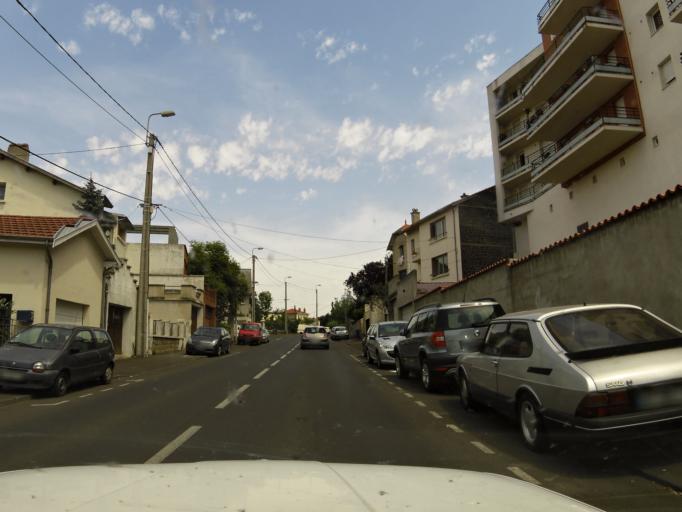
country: FR
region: Auvergne
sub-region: Departement du Puy-de-Dome
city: Beaumont
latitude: 45.7572
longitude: 3.0823
